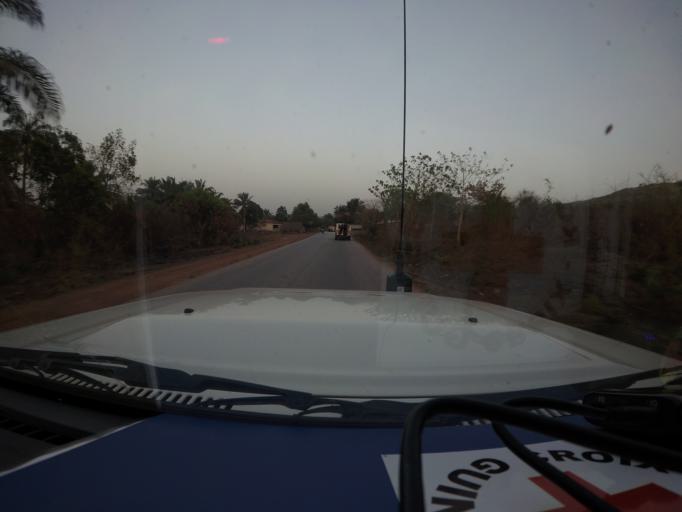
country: GN
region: Kindia
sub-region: Kindia
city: Kindia
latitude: 9.9016
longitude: -13.0298
